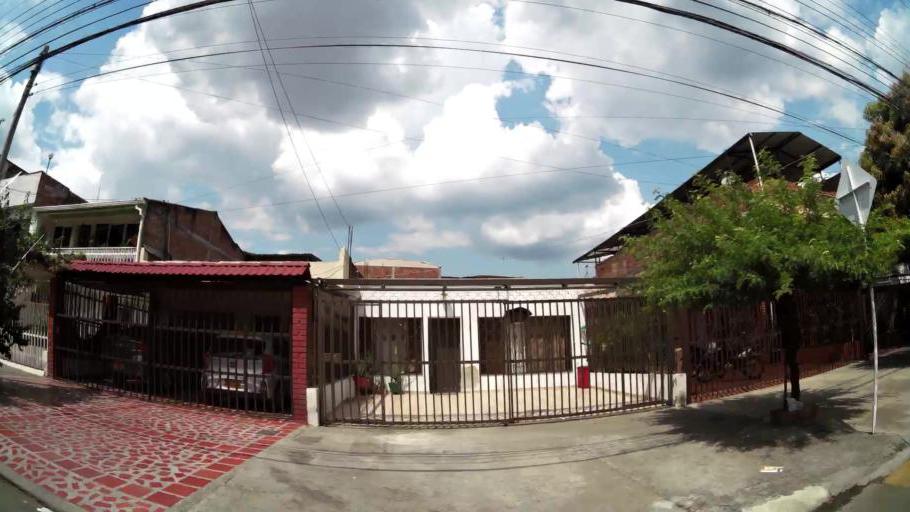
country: CO
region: Valle del Cauca
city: Cali
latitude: 3.4840
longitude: -76.5030
